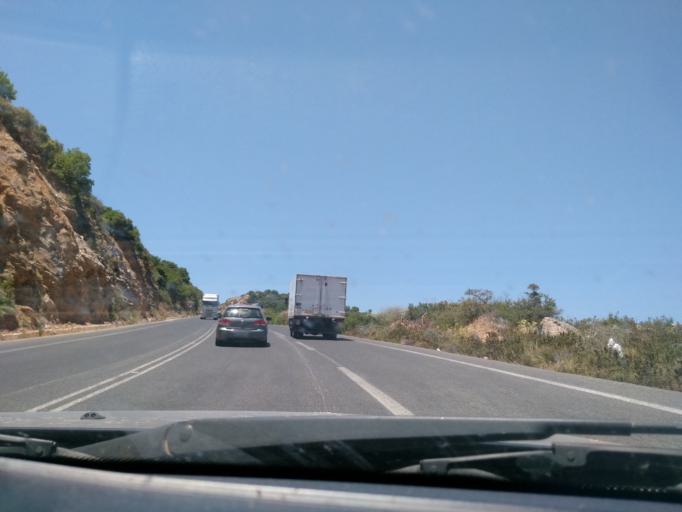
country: GR
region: Crete
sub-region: Nomos Rethymnis
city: Anogeia
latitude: 35.3867
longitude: 24.9167
